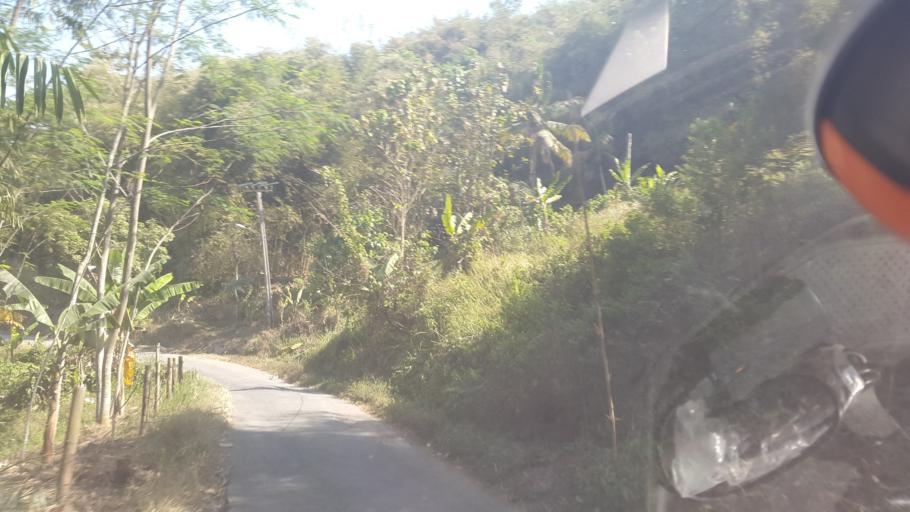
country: ID
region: West Java
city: Suryabakti
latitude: -6.9893
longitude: 106.8450
